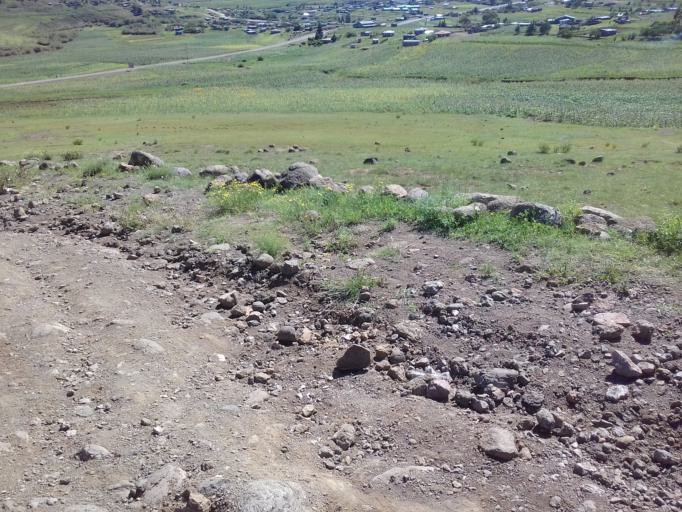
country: LS
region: Thaba-Tseka
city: Thaba-Tseka
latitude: -29.5225
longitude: 28.5830
